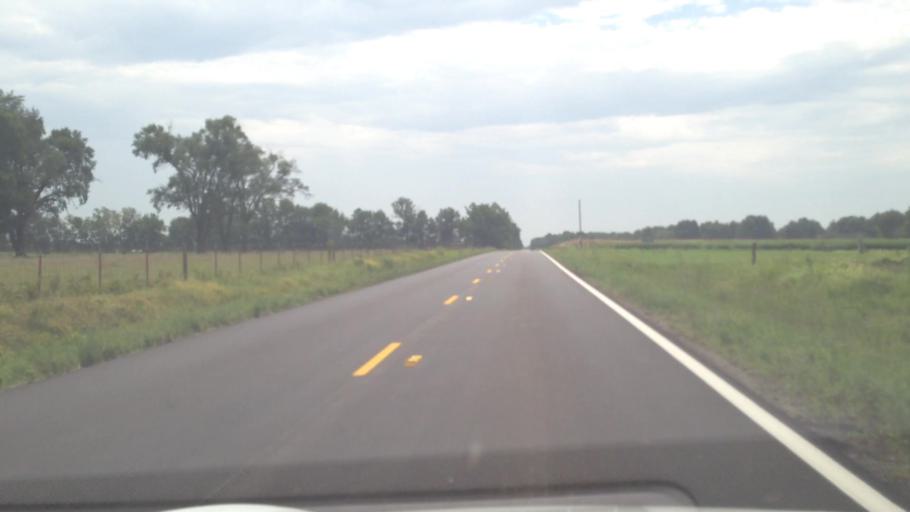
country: US
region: Kansas
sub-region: Crawford County
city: Girard
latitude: 37.5306
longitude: -94.9606
